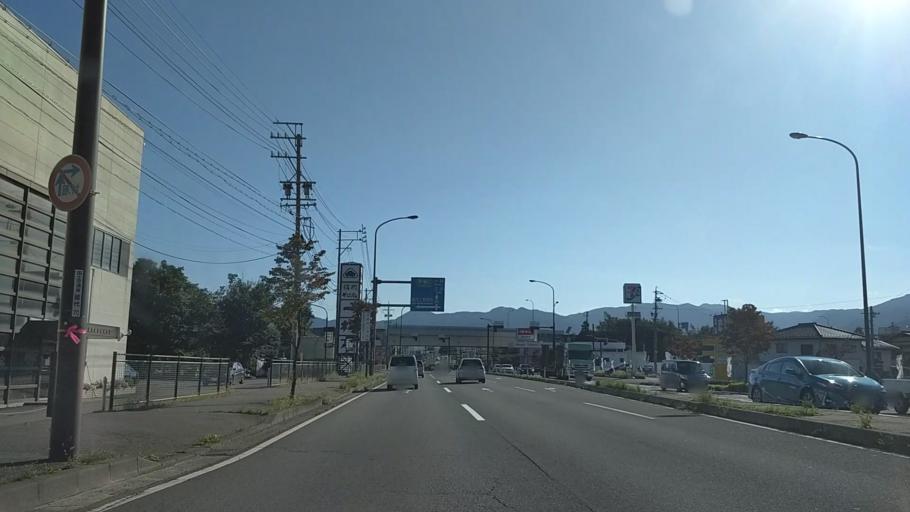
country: JP
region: Nagano
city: Nagano-shi
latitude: 36.5536
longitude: 138.1372
